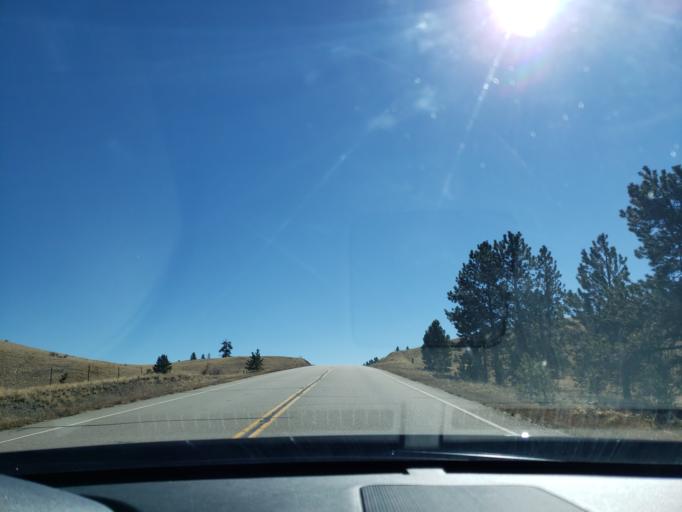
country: US
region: Colorado
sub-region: Chaffee County
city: Buena Vista
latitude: 38.8928
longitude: -105.6884
